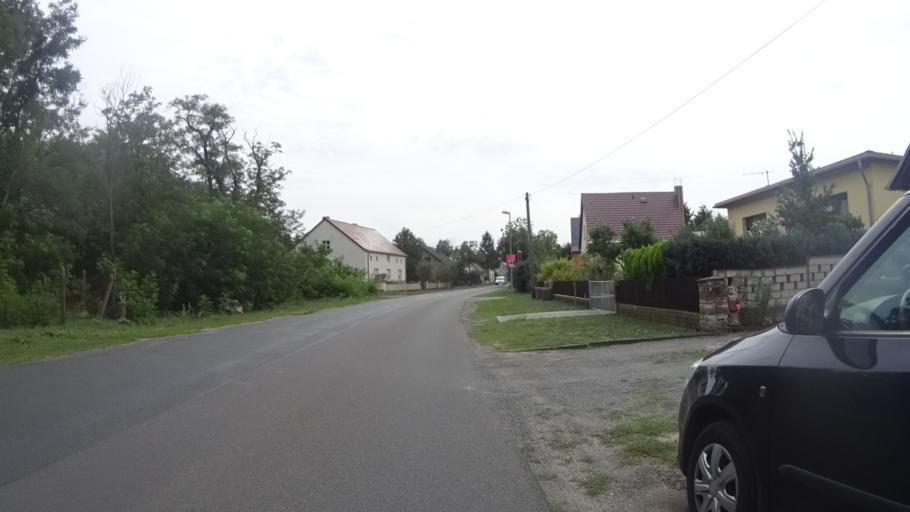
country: DE
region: Brandenburg
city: Borkwalde
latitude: 52.2902
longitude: 12.8259
